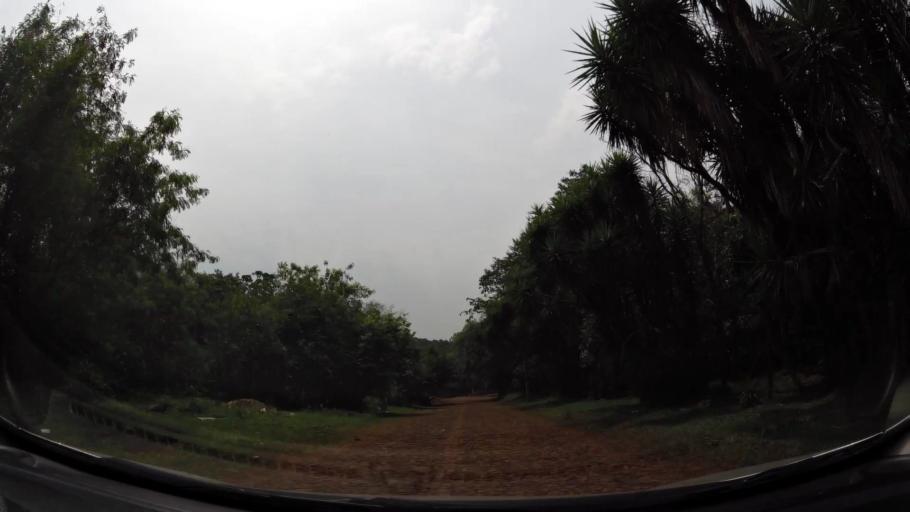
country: PY
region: Alto Parana
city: Presidente Franco
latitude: -25.5614
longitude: -54.6342
